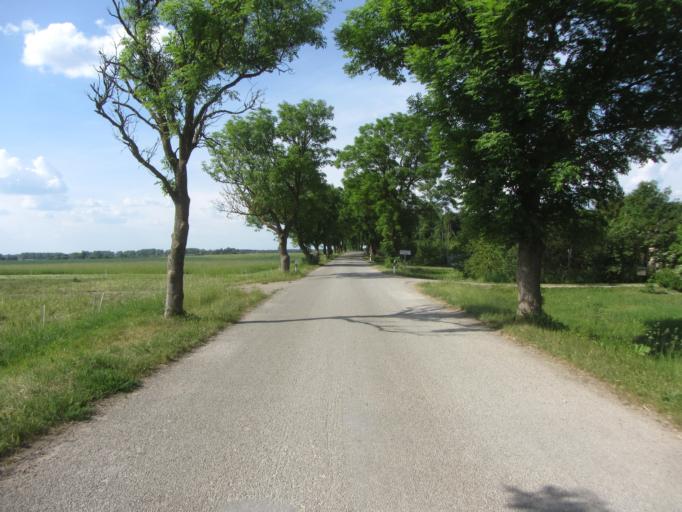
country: LT
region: Kauno apskritis
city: Jonava
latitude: 55.1833
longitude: 24.3749
